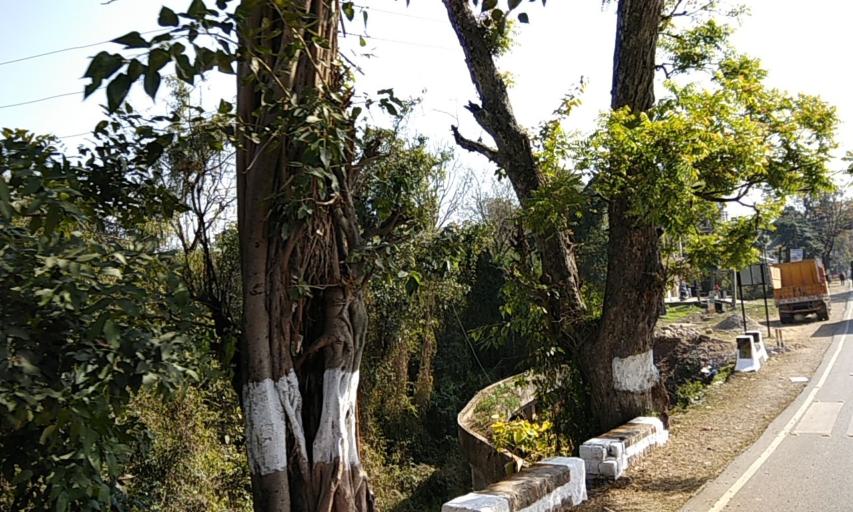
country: IN
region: Himachal Pradesh
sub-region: Kangra
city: Yol
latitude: 32.2209
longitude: 76.1754
